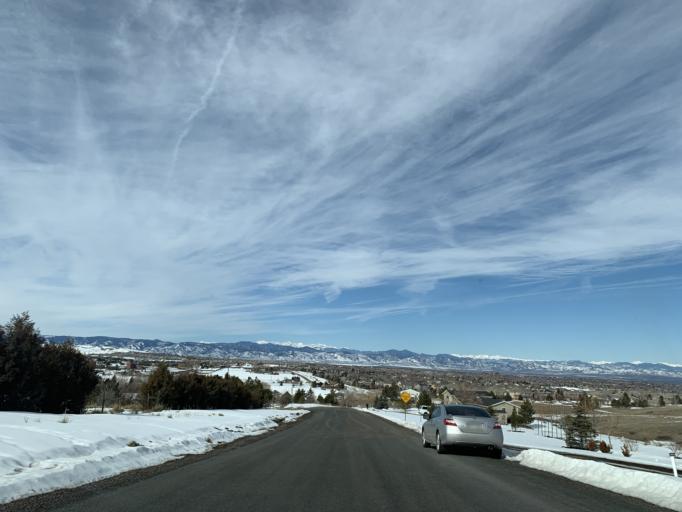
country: US
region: Colorado
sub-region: Douglas County
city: Carriage Club
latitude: 39.5205
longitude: -104.8967
